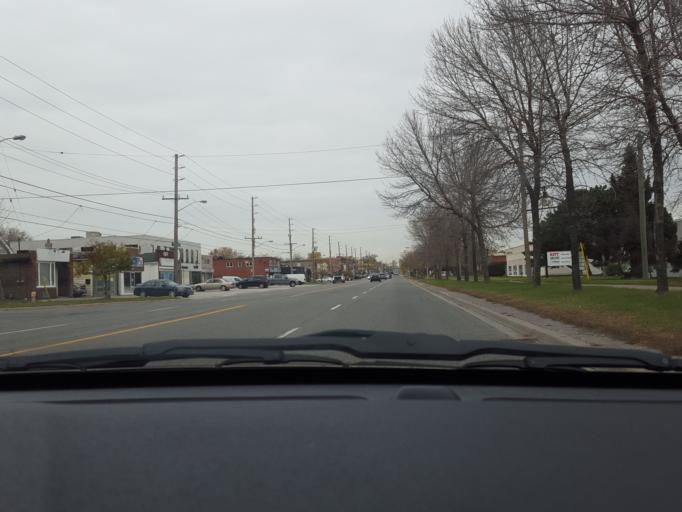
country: CA
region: Ontario
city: Etobicoke
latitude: 43.5971
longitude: -79.5431
